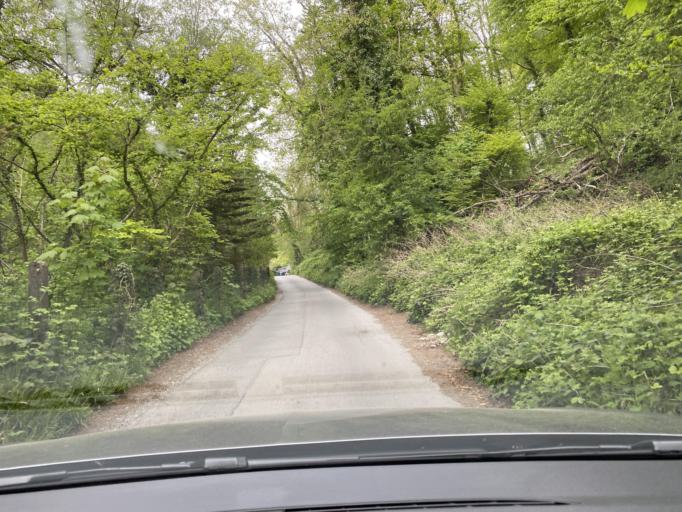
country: DE
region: North Rhine-Westphalia
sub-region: Regierungsbezirk Dusseldorf
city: Ratingen
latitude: 51.3186
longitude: 6.9062
